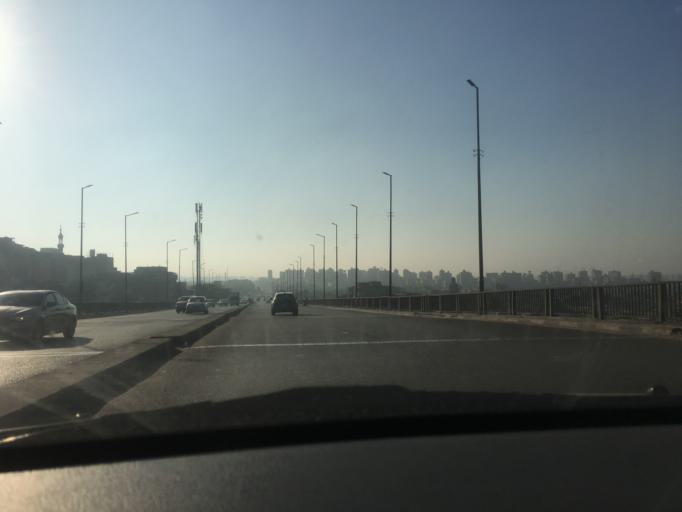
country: EG
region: Muhafazat al Qahirah
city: Cairo
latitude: 30.0239
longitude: 31.2628
